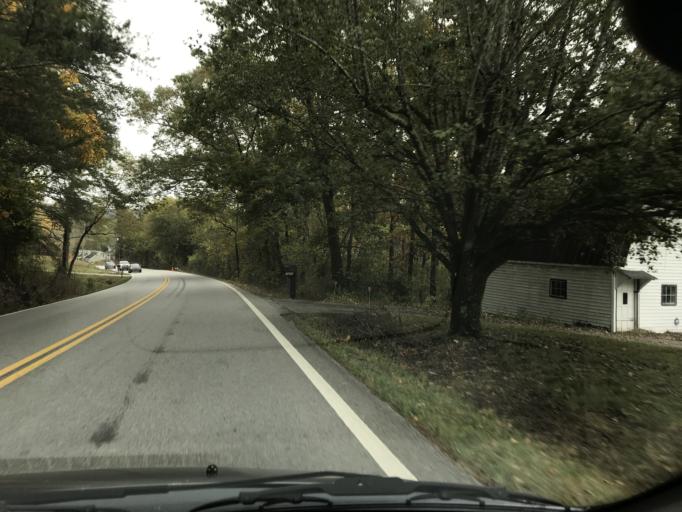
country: US
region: Tennessee
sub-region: Hamilton County
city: Lakesite
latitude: 35.1828
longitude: -85.0574
